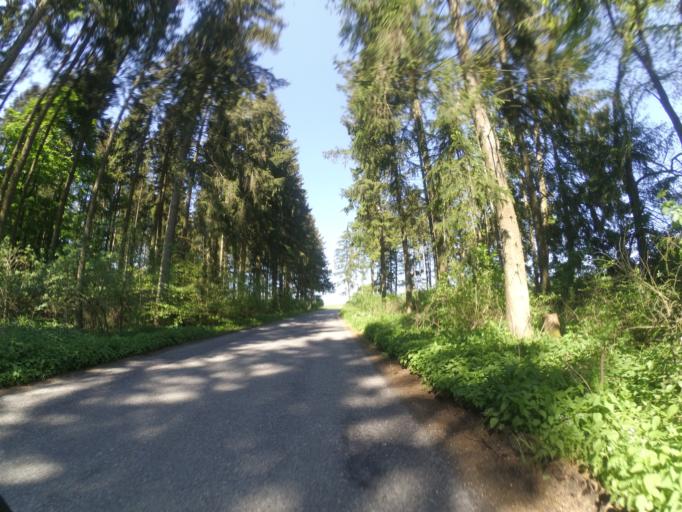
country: DE
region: Baden-Wuerttemberg
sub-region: Tuebingen Region
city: Dornstadt
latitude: 48.4606
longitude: 9.8829
